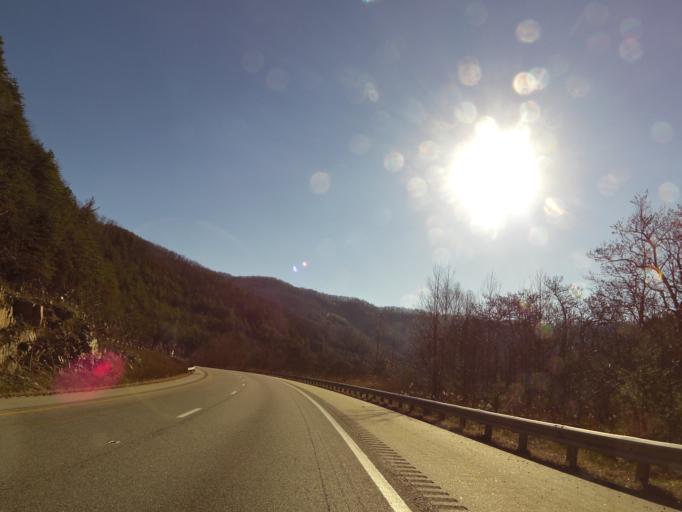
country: US
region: North Carolina
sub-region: Haywood County
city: Cove Creek
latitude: 35.7179
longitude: -83.0377
